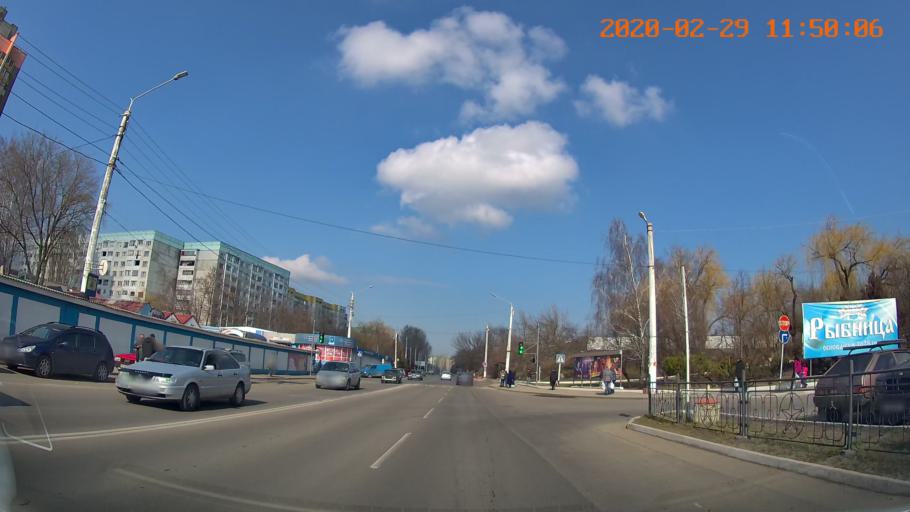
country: MD
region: Telenesti
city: Ribnita
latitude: 47.7557
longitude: 28.9915
